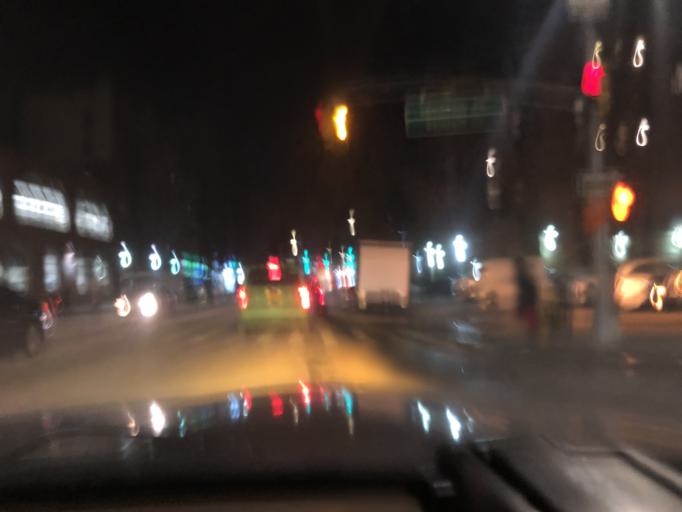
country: US
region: New York
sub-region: New York County
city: Inwood
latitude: 40.8594
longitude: -73.9313
